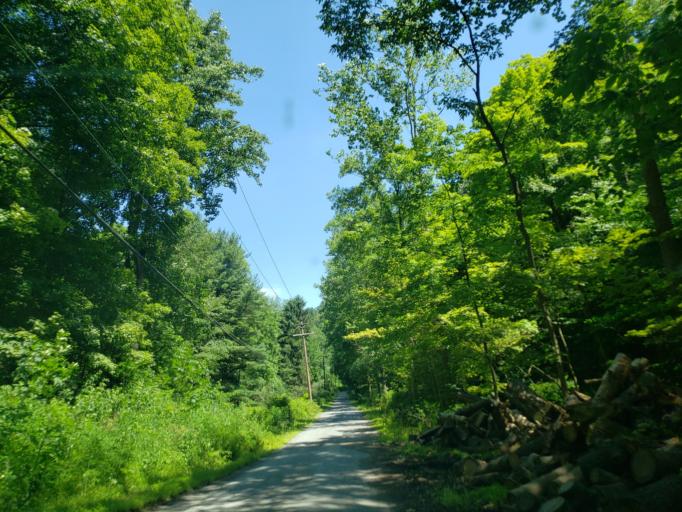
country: US
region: Pennsylvania
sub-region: Allegheny County
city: Emsworth
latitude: 40.5272
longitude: -80.1141
